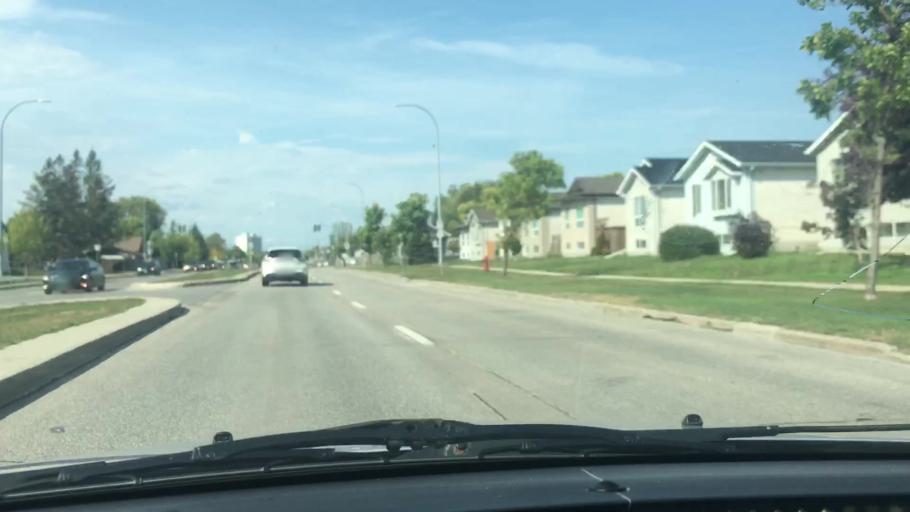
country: CA
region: Manitoba
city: Winnipeg
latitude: 49.8240
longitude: -97.1016
